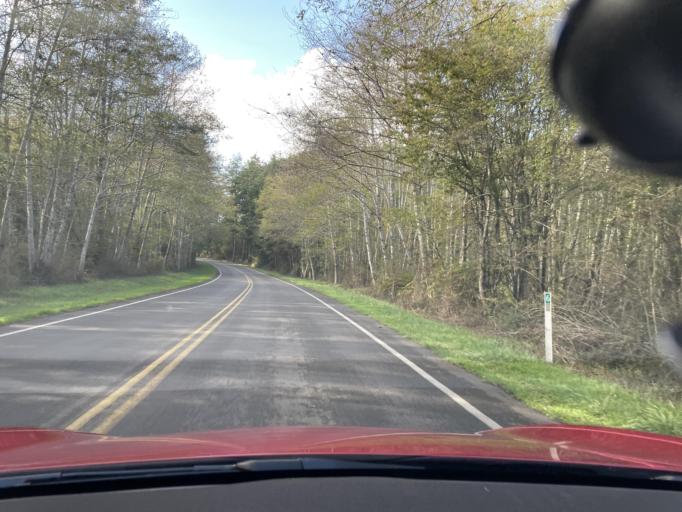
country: US
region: Washington
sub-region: San Juan County
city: Friday Harbor
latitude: 48.4690
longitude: -123.0146
